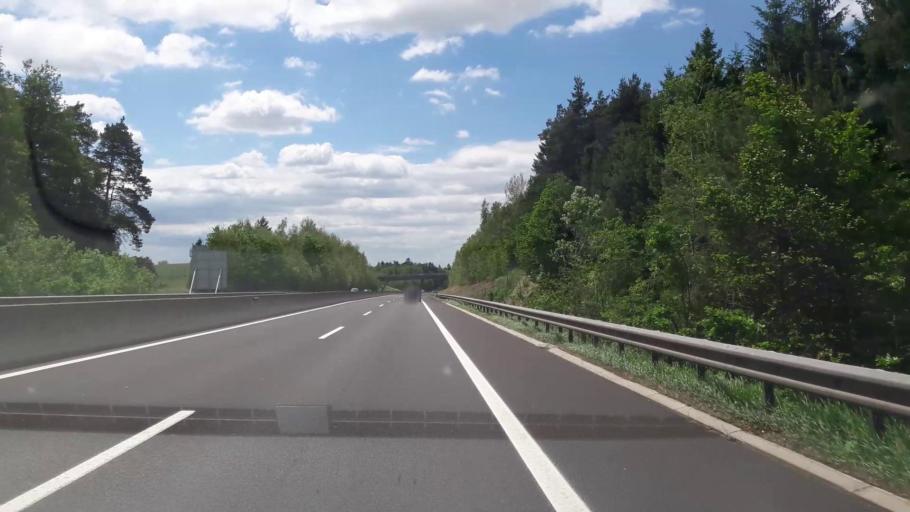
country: AT
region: Burgenland
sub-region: Politischer Bezirk Oberwart
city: Grafenschachen
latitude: 47.3615
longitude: 16.0831
